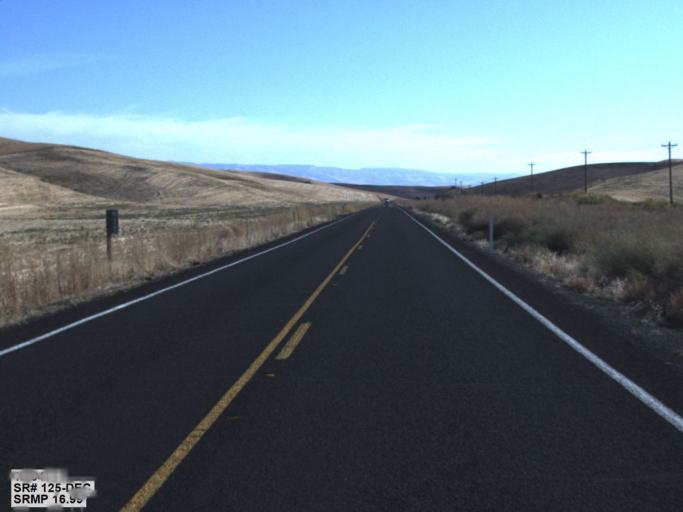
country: US
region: Washington
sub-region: Walla Walla County
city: Walla Walla
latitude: 46.2129
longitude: -118.3917
